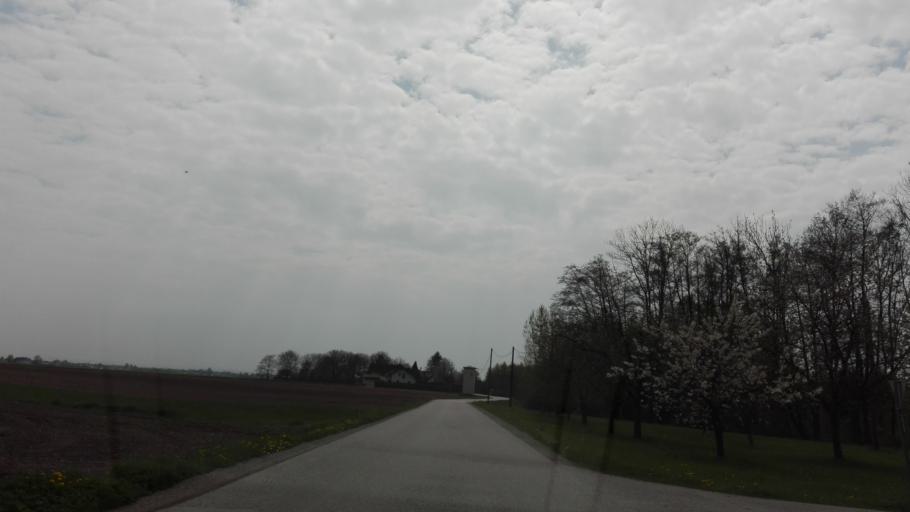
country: AT
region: Upper Austria
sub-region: Politischer Bezirk Perg
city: Perg
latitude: 48.2423
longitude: 14.5977
